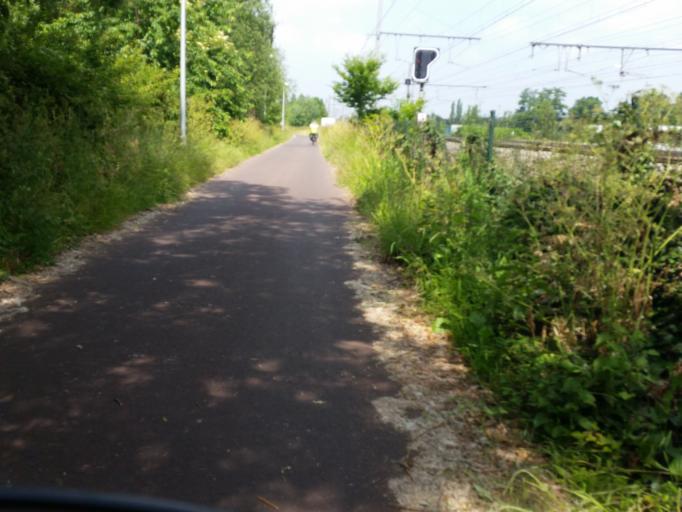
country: BE
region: Flanders
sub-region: Provincie Antwerpen
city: Hove
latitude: 51.1365
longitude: 4.4750
